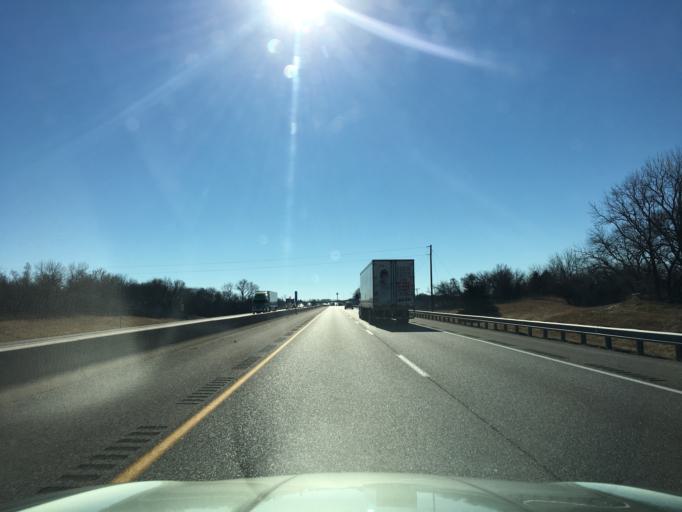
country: US
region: Kansas
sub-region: Sumner County
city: Belle Plaine
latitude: 37.3859
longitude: -97.3248
